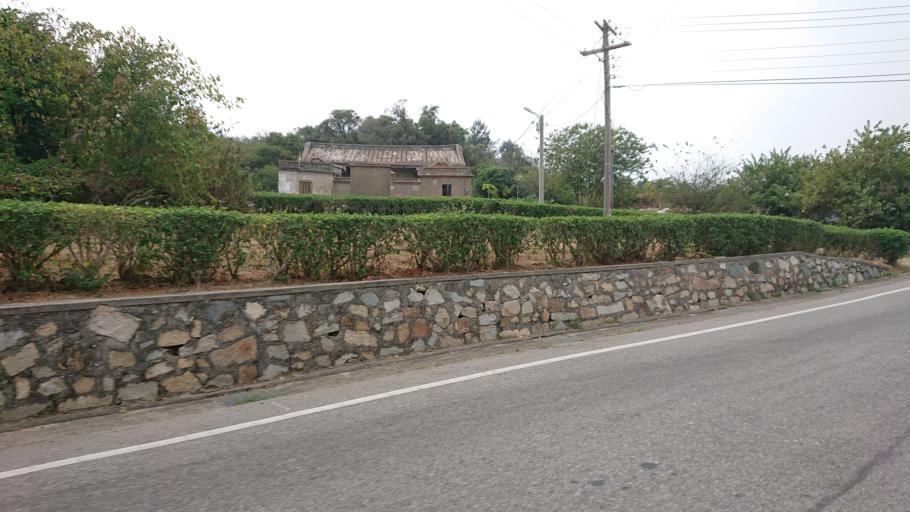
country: TW
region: Fukien
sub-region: Kinmen
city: Jincheng
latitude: 24.4458
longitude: 118.2525
